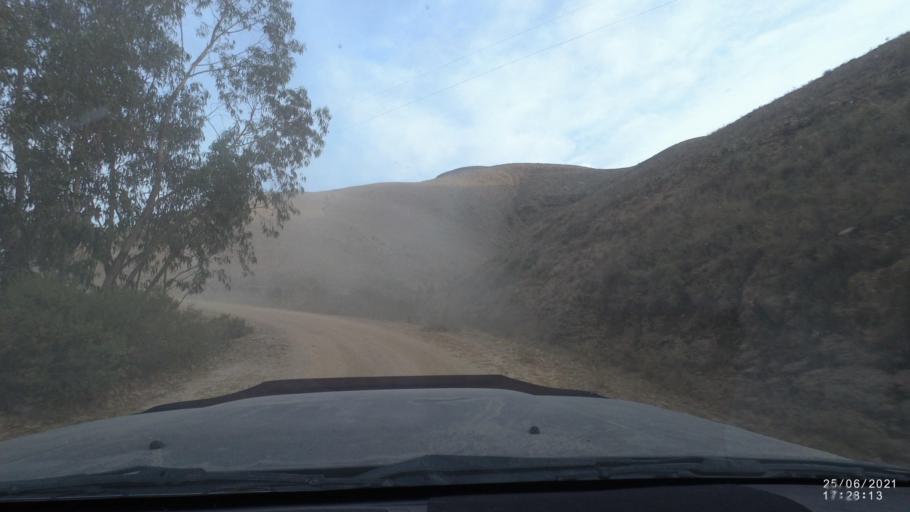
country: BO
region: Cochabamba
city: Mizque
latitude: -17.9257
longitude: -65.6707
